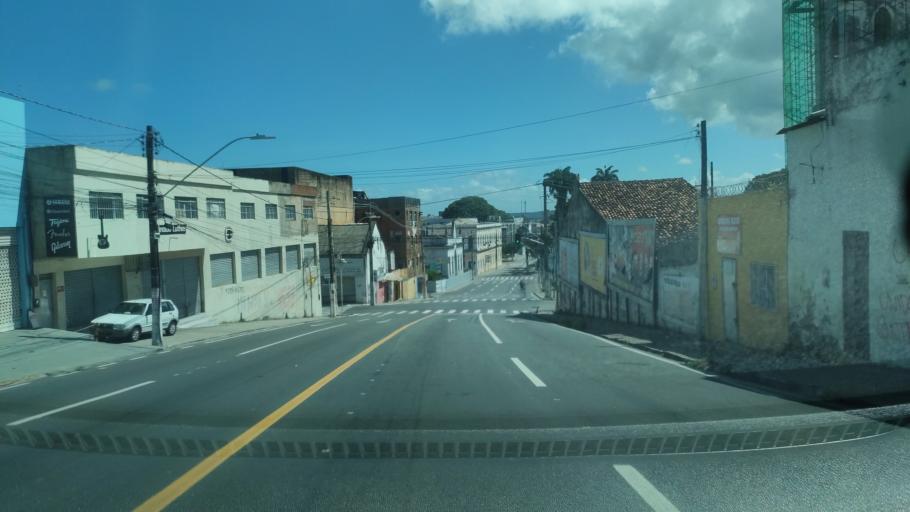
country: BR
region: Alagoas
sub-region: Maceio
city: Maceio
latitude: -9.6600
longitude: -35.7380
